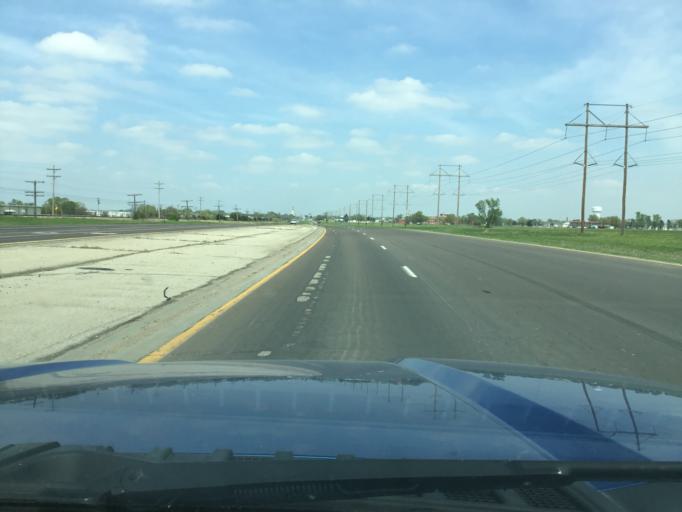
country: US
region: Kansas
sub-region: Shawnee County
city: Topeka
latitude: 38.9356
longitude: -95.6871
